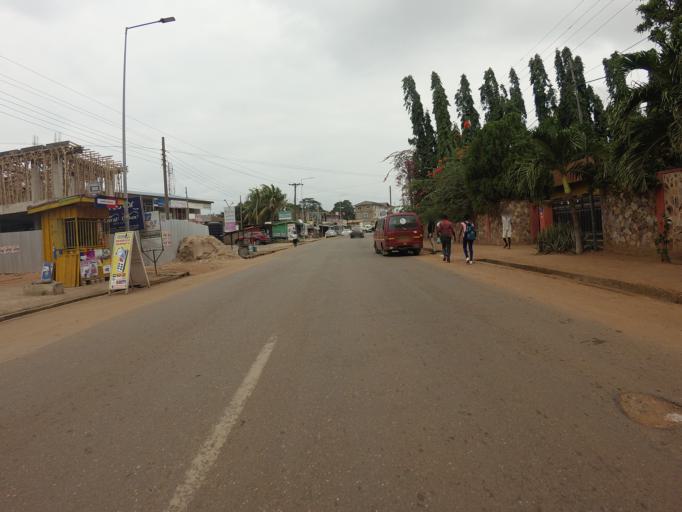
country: GH
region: Greater Accra
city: Dome
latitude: 5.6653
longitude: -0.2046
